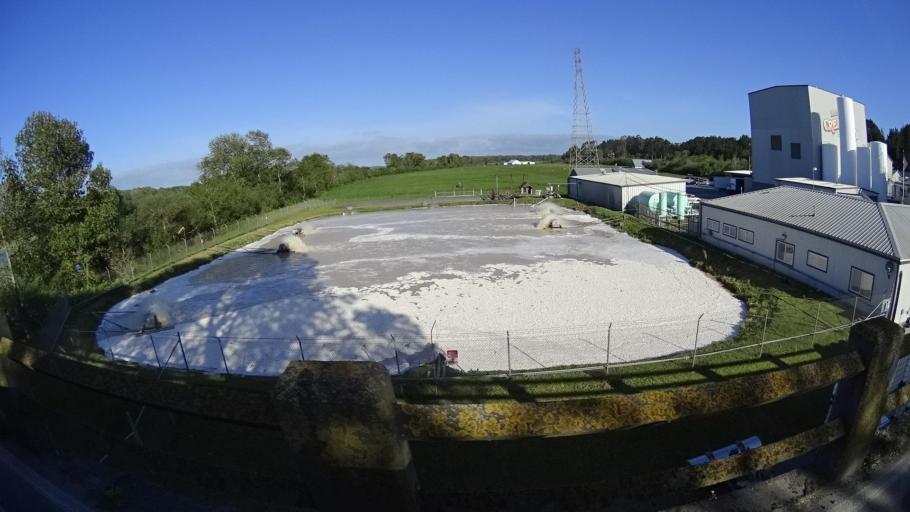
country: US
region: California
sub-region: Humboldt County
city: Fortuna
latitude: 40.6151
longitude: -124.2027
